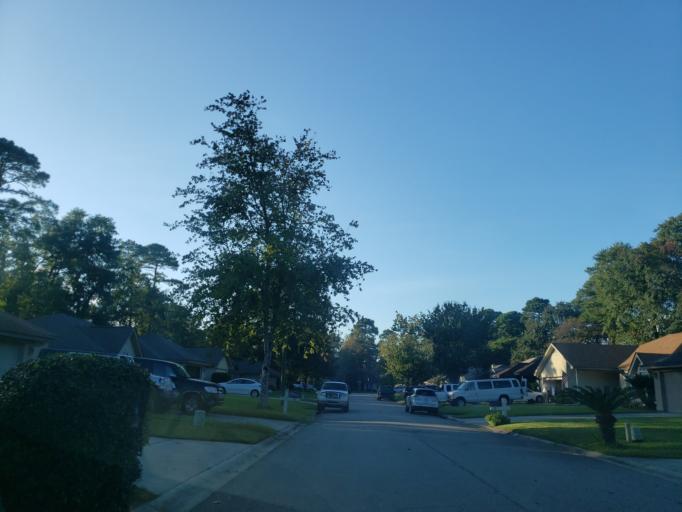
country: US
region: Georgia
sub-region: Chatham County
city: Isle of Hope
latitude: 31.9895
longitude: -81.0711
